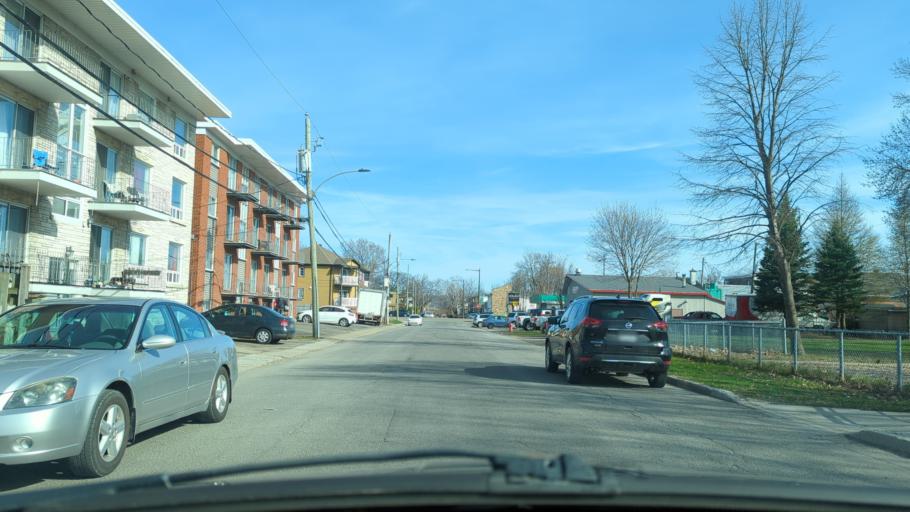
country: CA
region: Quebec
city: Quebec
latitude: 46.8493
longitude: -71.2098
